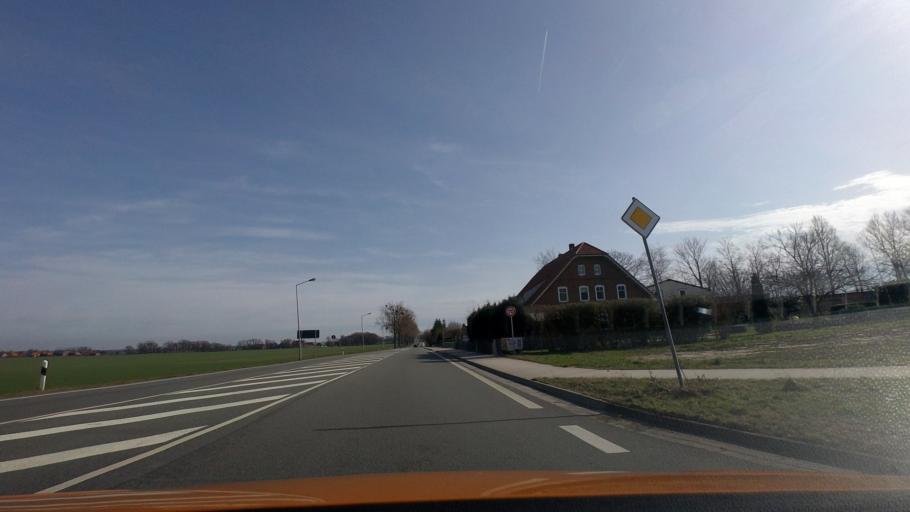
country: DE
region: Lower Saxony
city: Lauenhagen
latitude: 52.3302
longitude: 9.2370
